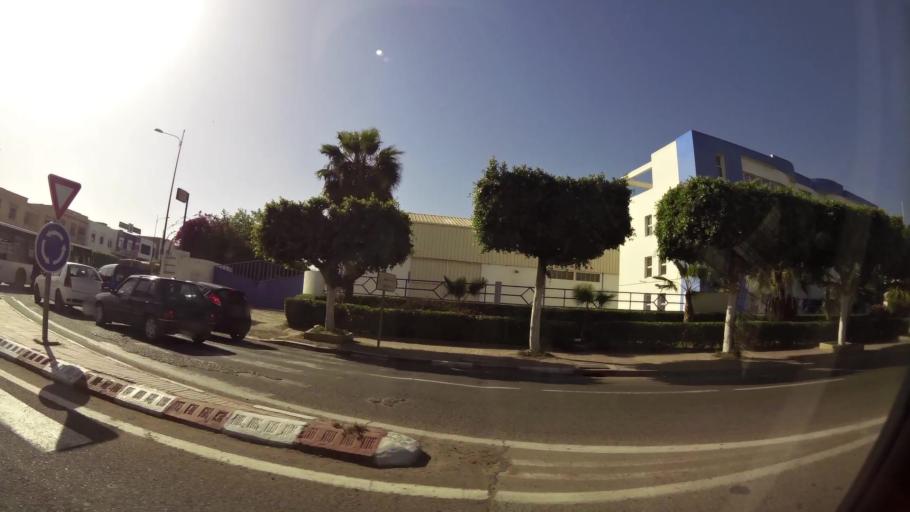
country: MA
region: Souss-Massa-Draa
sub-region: Inezgane-Ait Mellou
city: Inezgane
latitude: 30.3833
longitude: -9.5192
